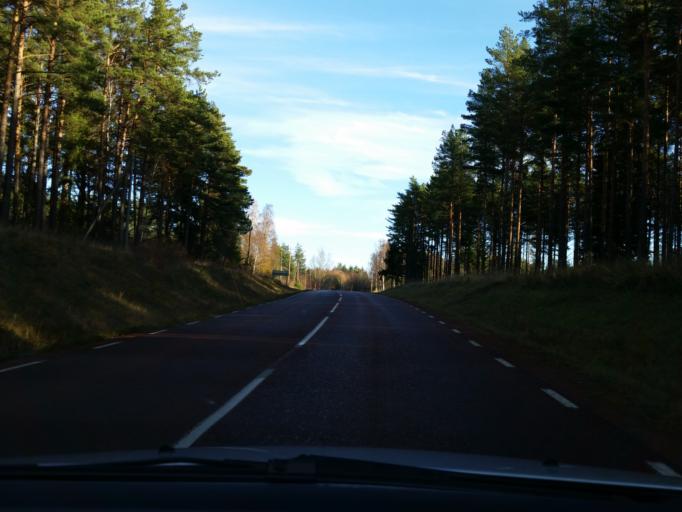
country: AX
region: Alands landsbygd
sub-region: Finstroem
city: Finstroem
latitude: 60.3056
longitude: 19.9561
